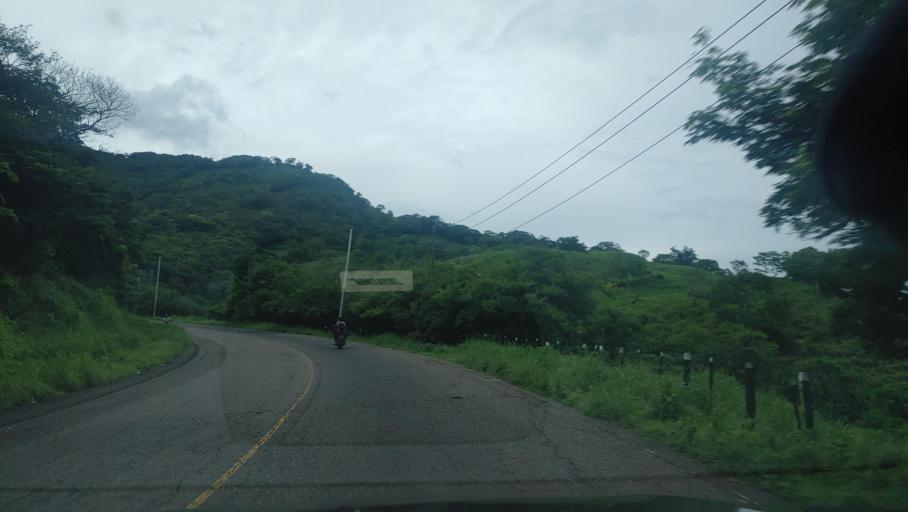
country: HN
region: Choluteca
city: Corpus
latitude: 13.3698
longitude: -87.0590
